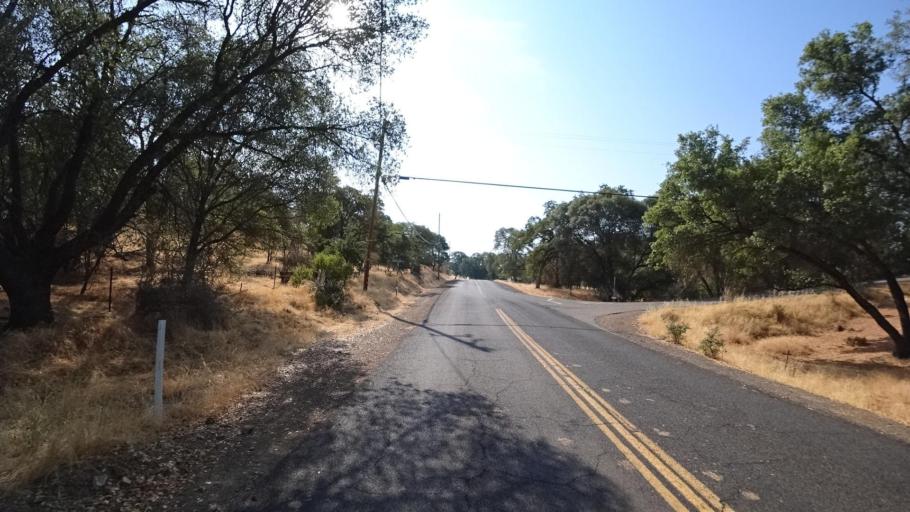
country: US
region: California
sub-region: Tuolumne County
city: Jamestown
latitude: 37.7171
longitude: -120.3256
